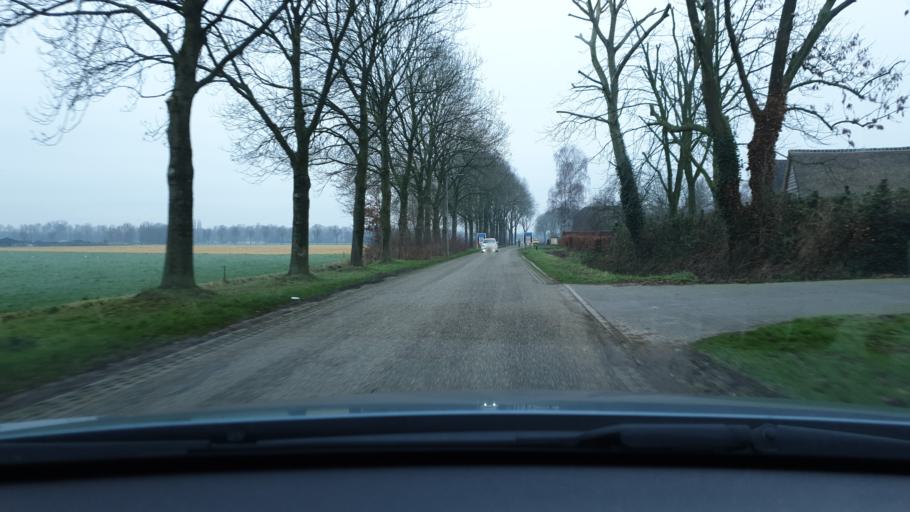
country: NL
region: Gelderland
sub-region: Gemeente Wijchen
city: Bergharen
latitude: 51.8507
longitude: 5.6763
